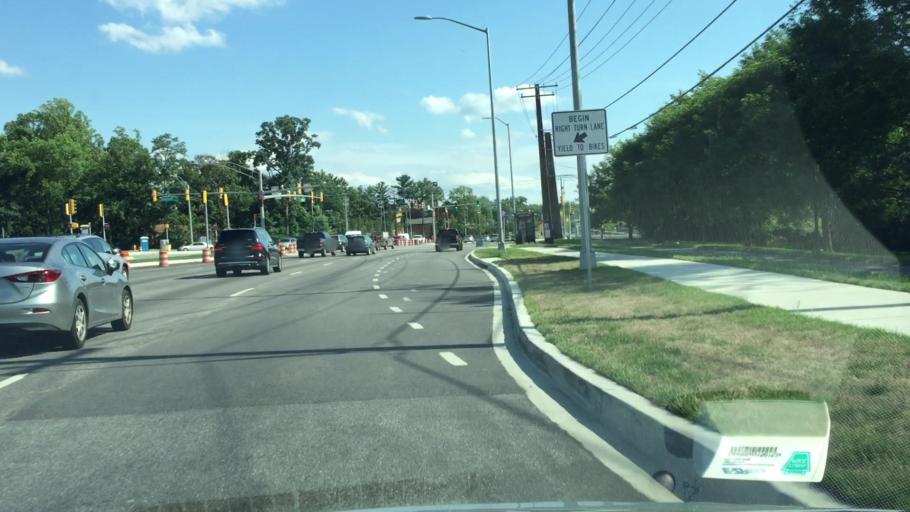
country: US
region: Maryland
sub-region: Montgomery County
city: Glenmont
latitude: 39.0591
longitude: -77.0504
